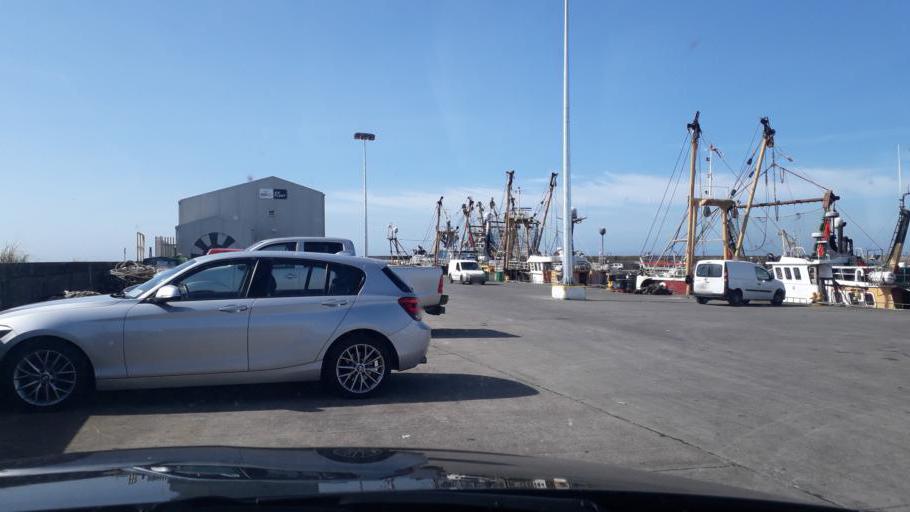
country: IE
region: Leinster
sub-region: Loch Garman
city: Loch Garman
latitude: 52.1720
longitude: -6.5869
